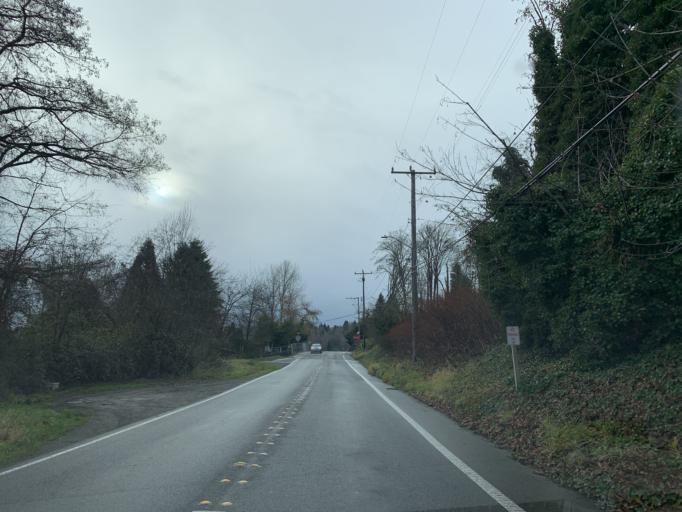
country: US
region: Washington
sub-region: King County
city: Tukwila
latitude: 47.4686
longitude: -122.2706
